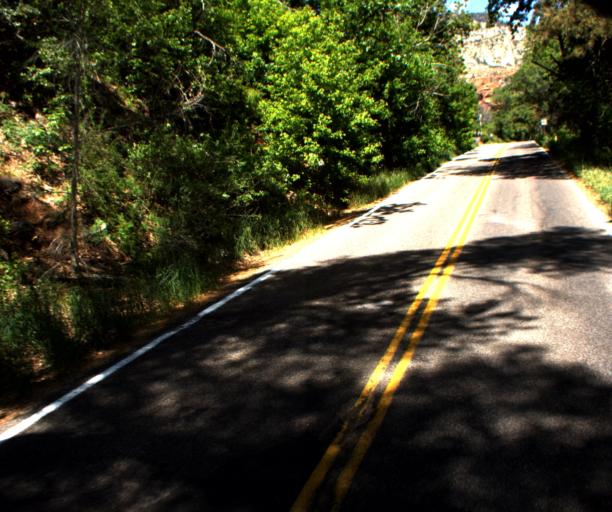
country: US
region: Arizona
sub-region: Coconino County
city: Sedona
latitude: 34.9370
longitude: -111.7474
